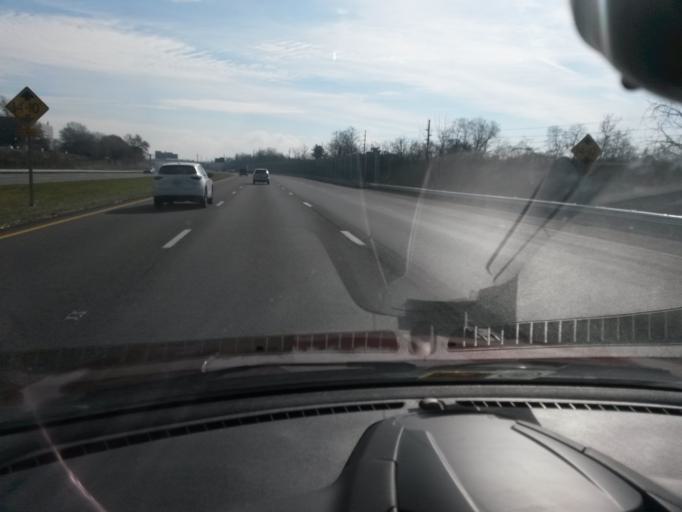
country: US
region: Virginia
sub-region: Roanoke County
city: Hollins
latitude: 37.3059
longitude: -79.9710
